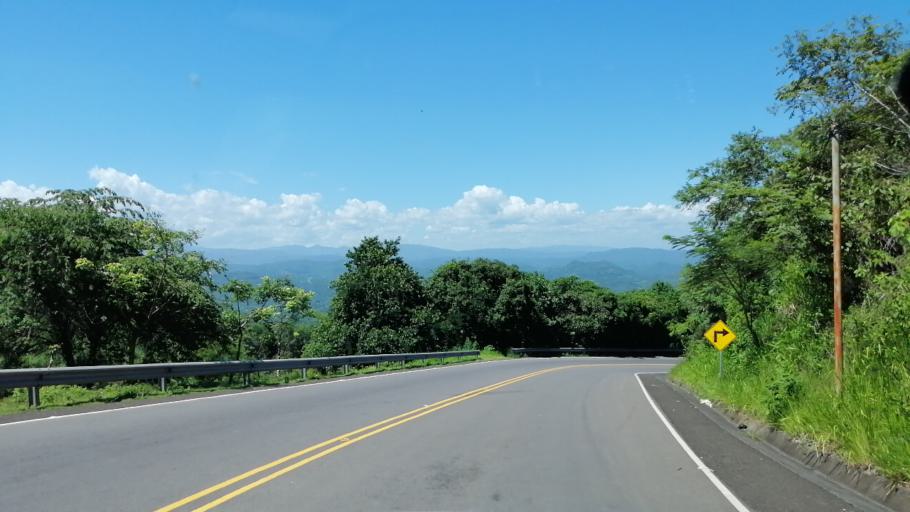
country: SV
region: San Miguel
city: Ciudad Barrios
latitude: 13.8154
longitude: -88.1867
